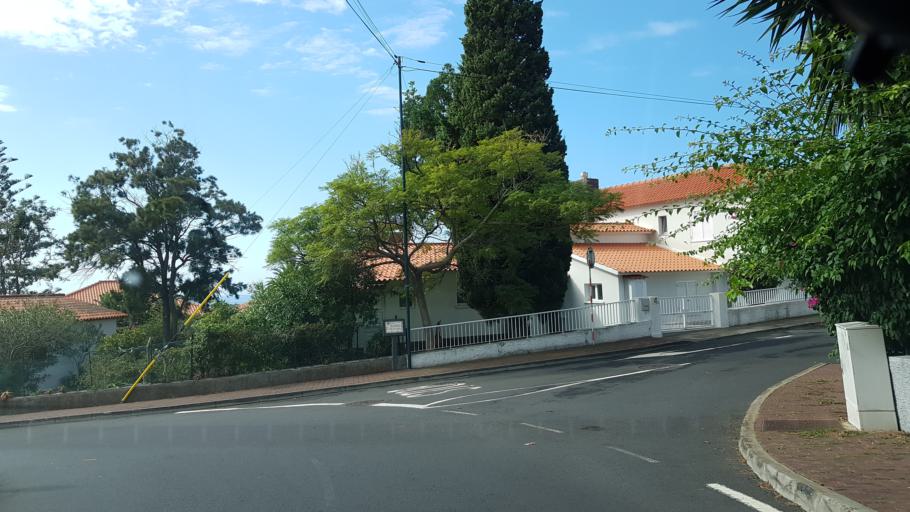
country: PT
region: Madeira
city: Canico
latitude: 32.6429
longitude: -16.8360
